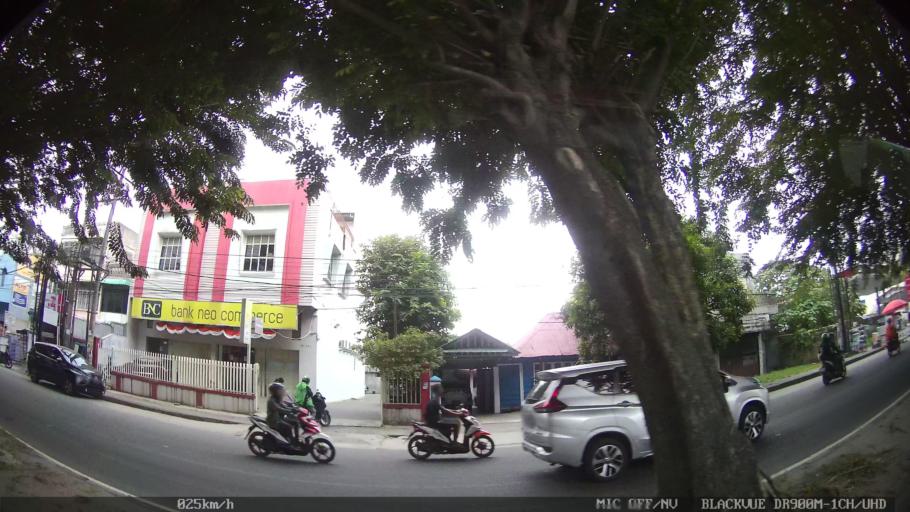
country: ID
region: North Sumatra
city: Medan
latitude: 3.5580
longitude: 98.6898
